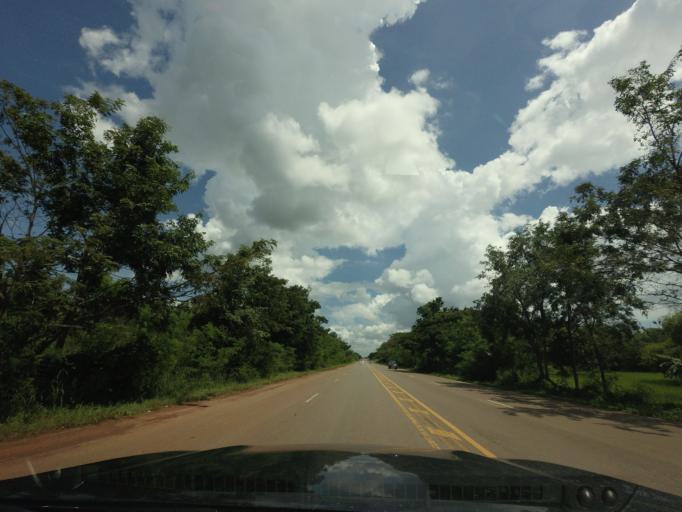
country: TH
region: Changwat Udon Thani
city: Ban Dung
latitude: 17.6811
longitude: 103.2279
